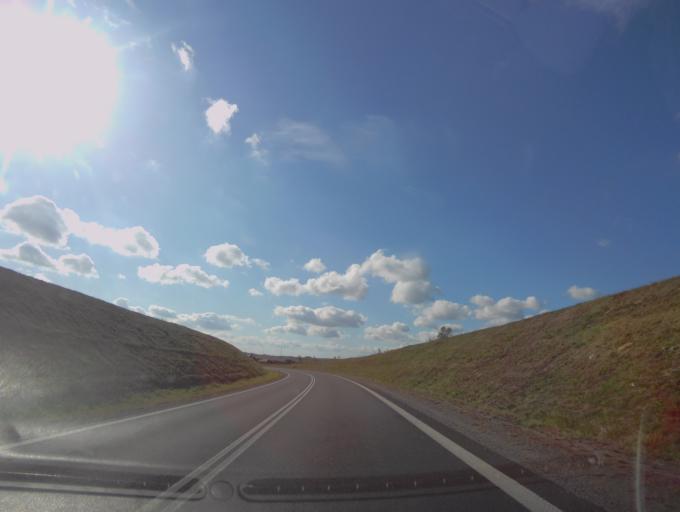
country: PL
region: Subcarpathian Voivodeship
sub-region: Powiat lezajski
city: Giedlarowa
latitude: 50.2456
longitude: 22.4087
